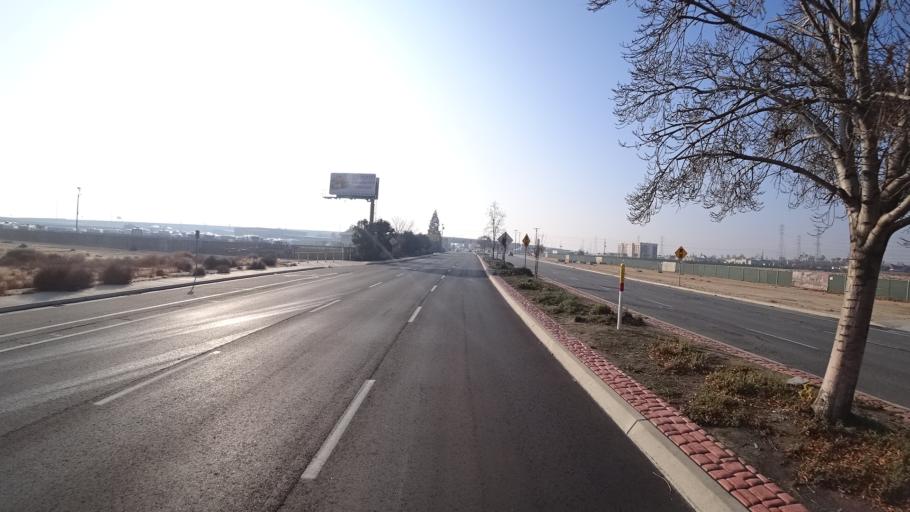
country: US
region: California
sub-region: Kern County
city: Greenacres
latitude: 35.3710
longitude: -119.0922
